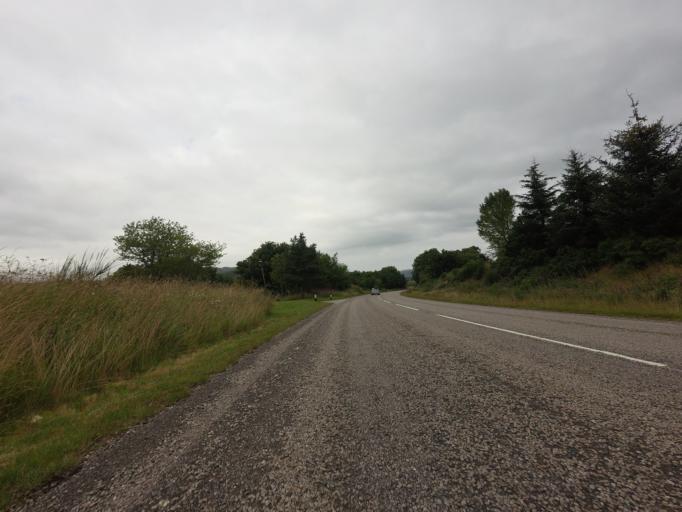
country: GB
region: Scotland
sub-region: Highland
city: Evanton
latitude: 57.9186
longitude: -4.3964
